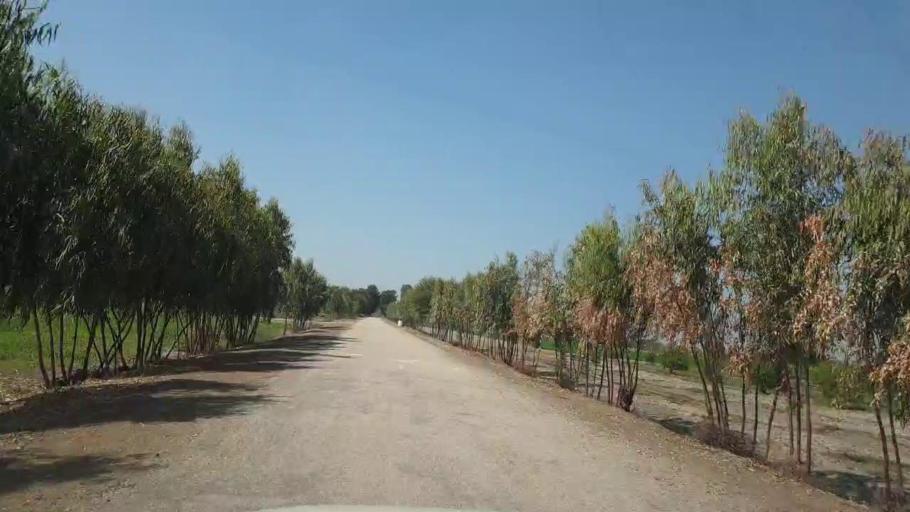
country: PK
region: Sindh
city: Kunri
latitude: 25.1283
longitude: 69.5144
